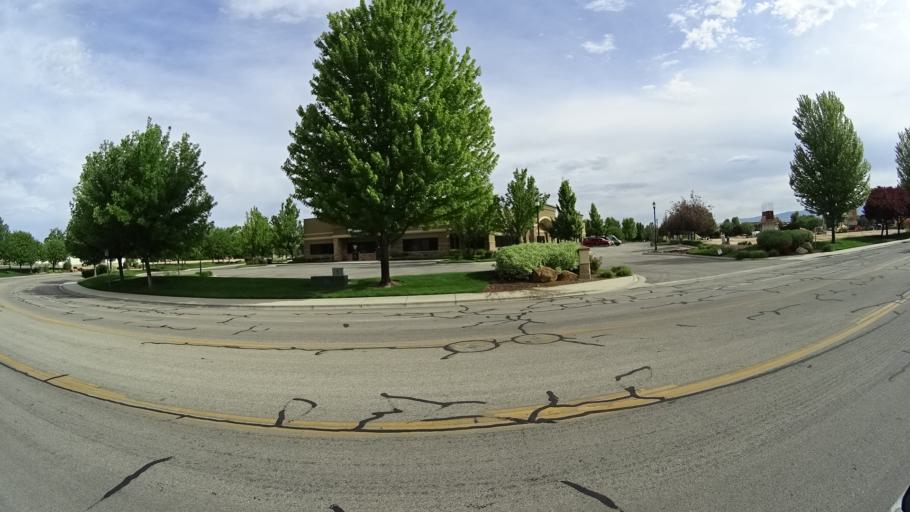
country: US
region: Idaho
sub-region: Ada County
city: Meridian
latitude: 43.5837
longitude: -116.3579
